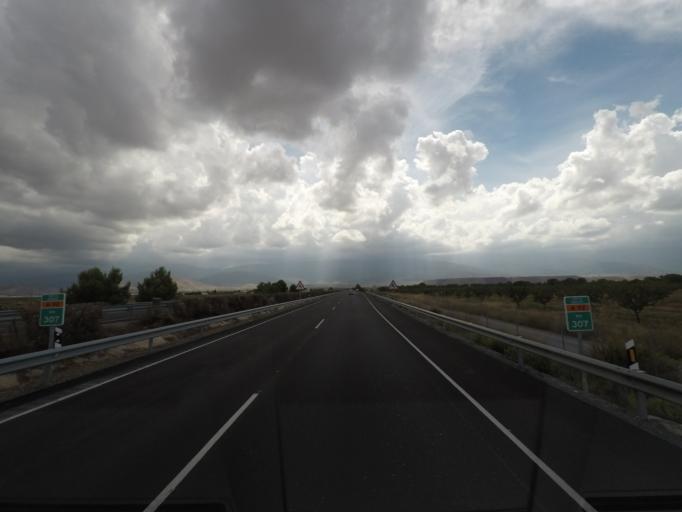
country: ES
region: Andalusia
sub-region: Provincia de Granada
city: Albunan
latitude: 37.2350
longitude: -3.0823
